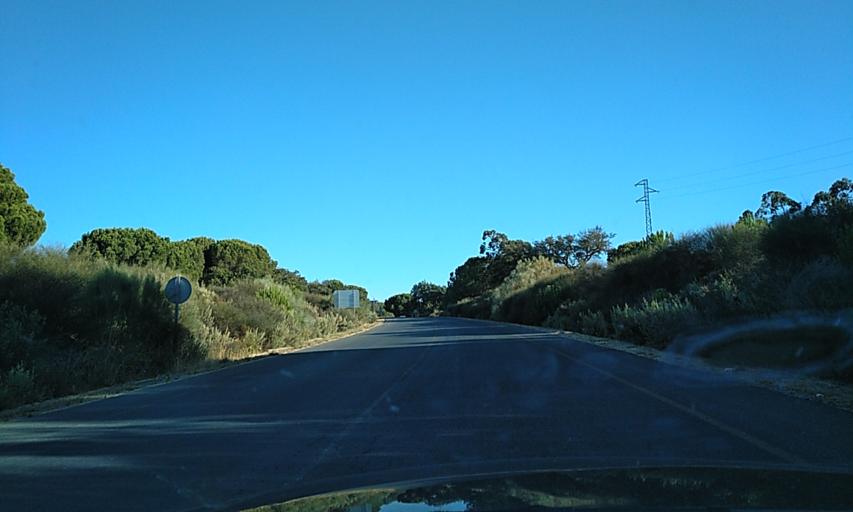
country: ES
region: Andalusia
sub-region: Provincia de Huelva
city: San Bartolome de la Torre
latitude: 37.4319
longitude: -7.1077
